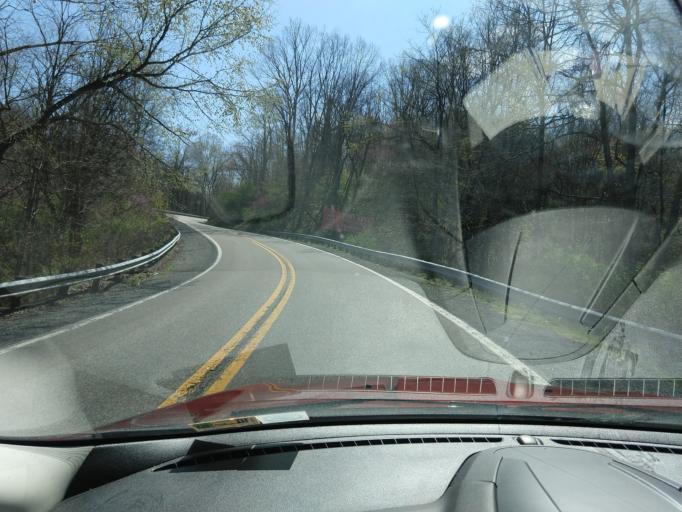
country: US
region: West Virginia
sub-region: Greenbrier County
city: Ronceverte
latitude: 37.7534
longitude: -80.5255
